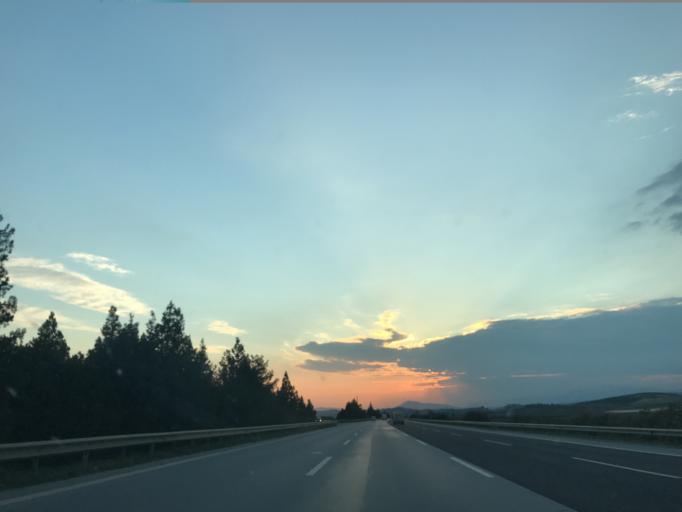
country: TR
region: Mersin
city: Yenice
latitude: 37.0128
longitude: 34.9929
